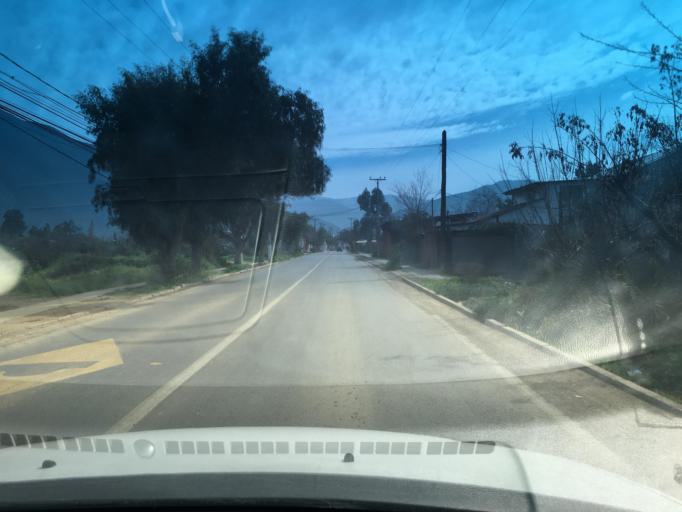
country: CL
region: Santiago Metropolitan
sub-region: Provincia de Chacabuco
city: Lampa
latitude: -33.0885
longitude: -70.9289
